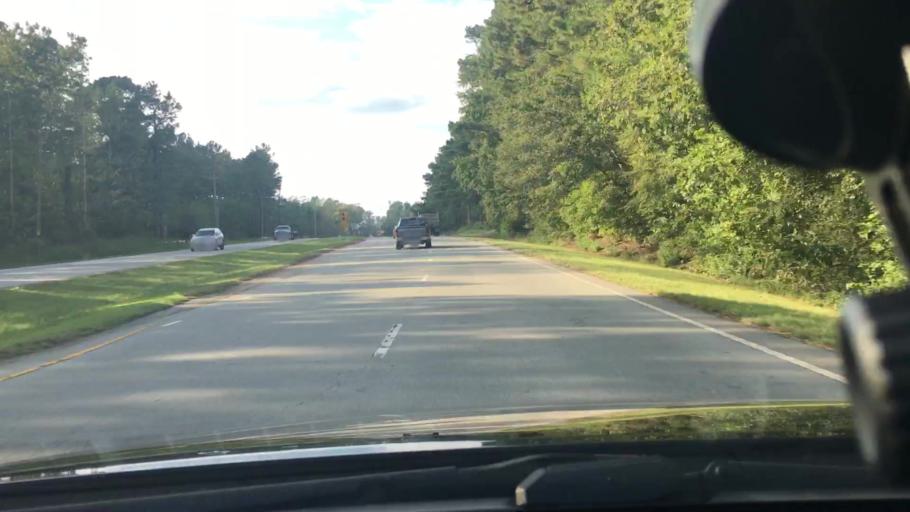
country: US
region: North Carolina
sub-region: Craven County
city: Vanceboro
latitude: 35.2841
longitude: -77.1256
